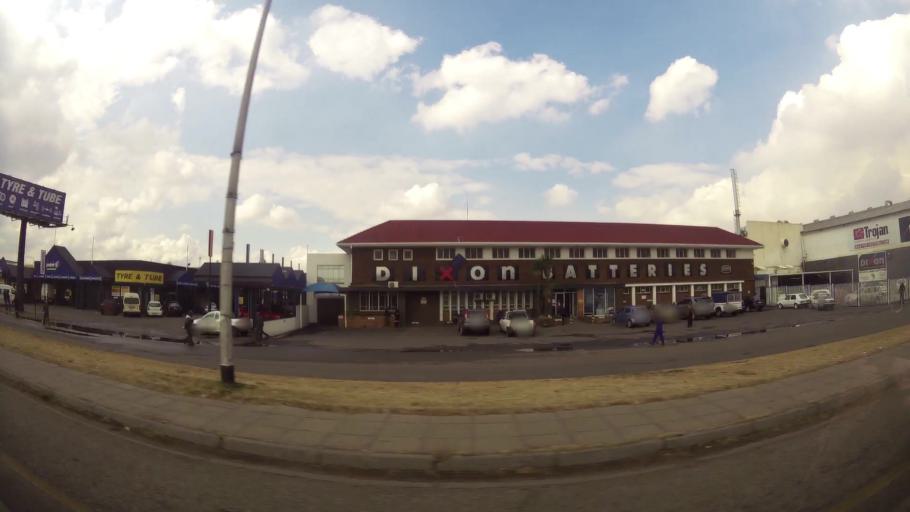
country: ZA
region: Gauteng
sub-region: Sedibeng District Municipality
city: Vereeniging
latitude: -26.6590
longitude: 27.9352
